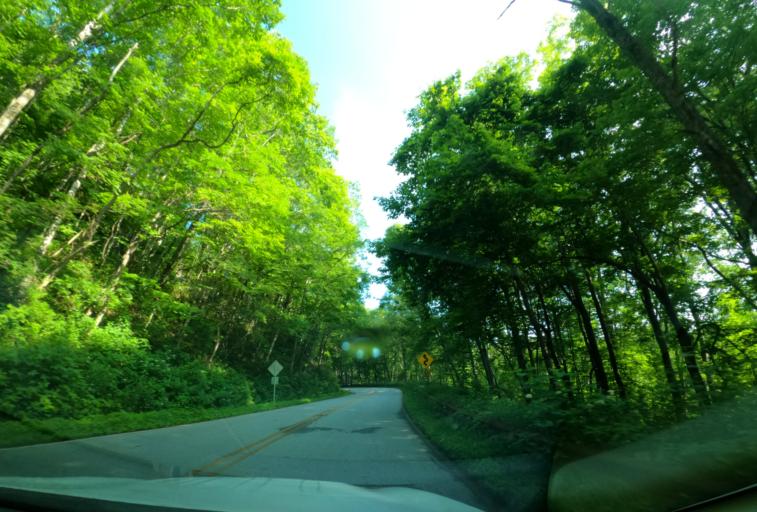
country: US
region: North Carolina
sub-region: Transylvania County
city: Brevard
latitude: 35.2591
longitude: -82.9204
